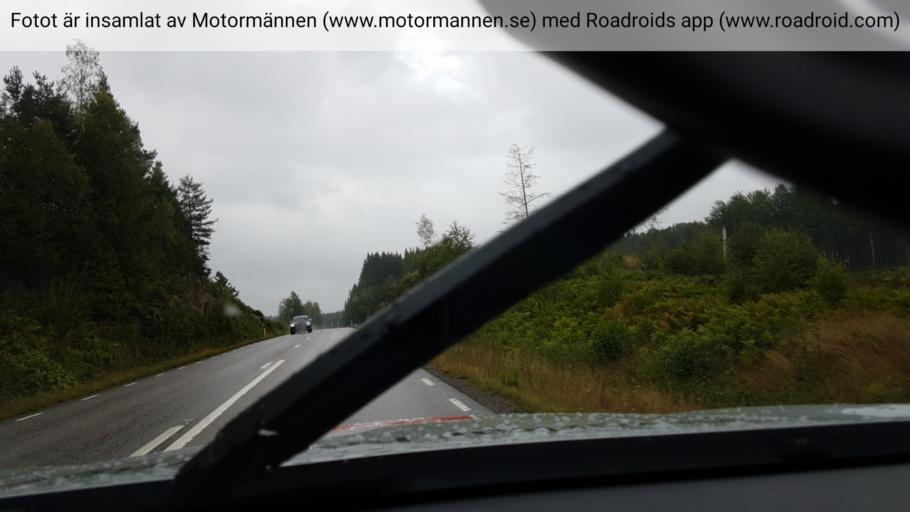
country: SE
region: Vaestra Goetaland
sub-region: Bengtsfors Kommun
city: Billingsfors
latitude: 58.9504
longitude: 12.2219
